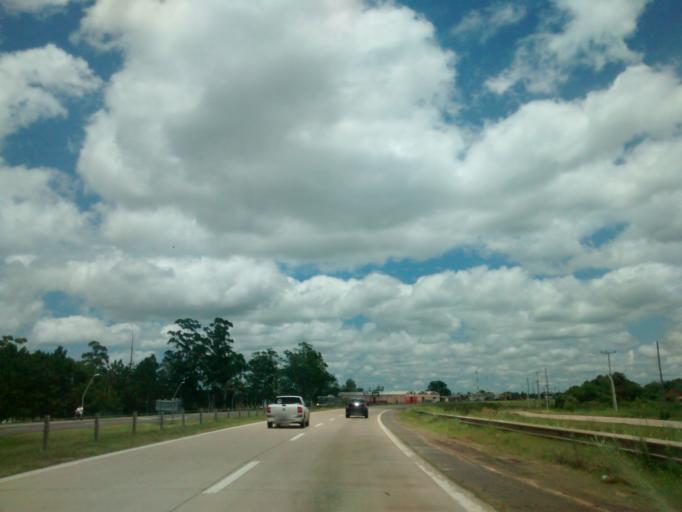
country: AR
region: Chaco
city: Fontana
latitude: -27.4117
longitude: -58.9940
